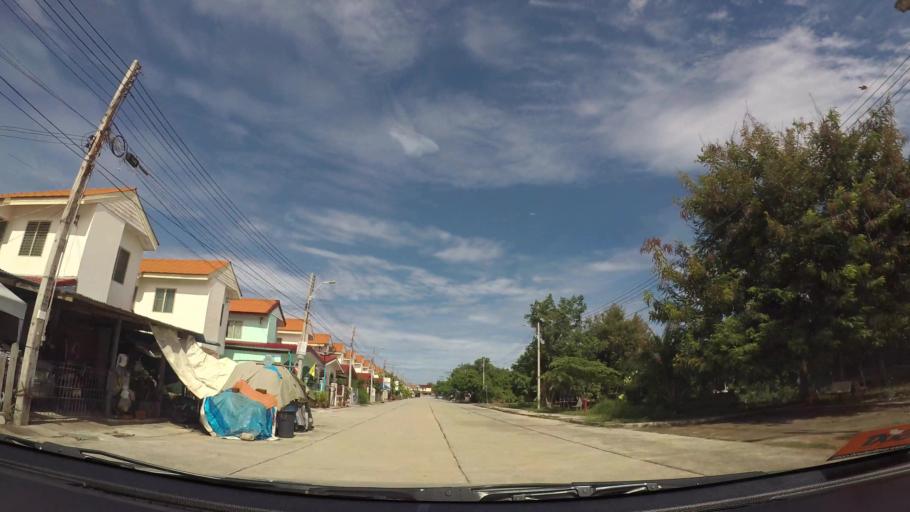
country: TH
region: Chon Buri
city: Sattahip
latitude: 12.6679
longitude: 100.9570
